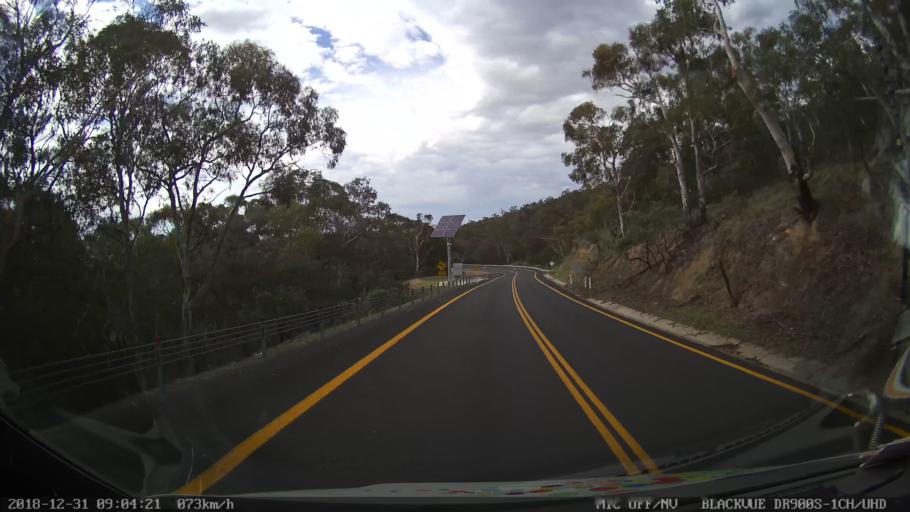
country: AU
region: New South Wales
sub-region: Snowy River
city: Jindabyne
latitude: -36.3533
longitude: 148.5865
